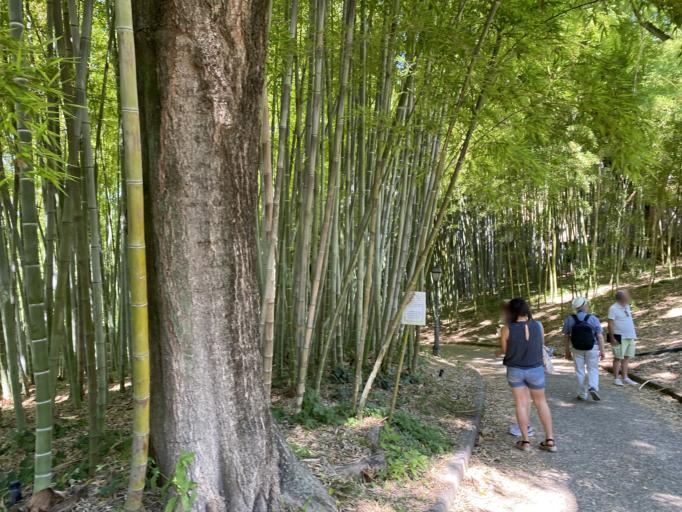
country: VA
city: Vatican City
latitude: 41.8895
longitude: 12.4639
